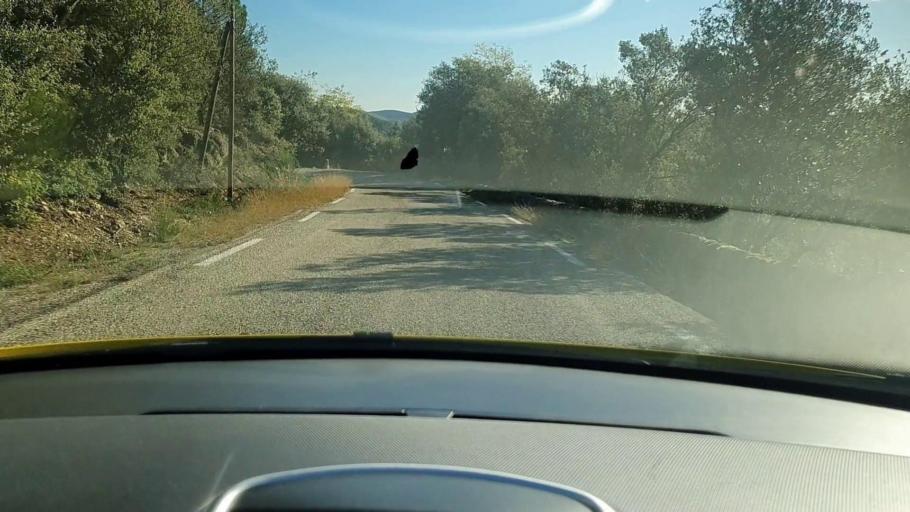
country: FR
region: Languedoc-Roussillon
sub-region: Departement du Gard
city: Lasalle
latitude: 44.0756
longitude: 3.8257
